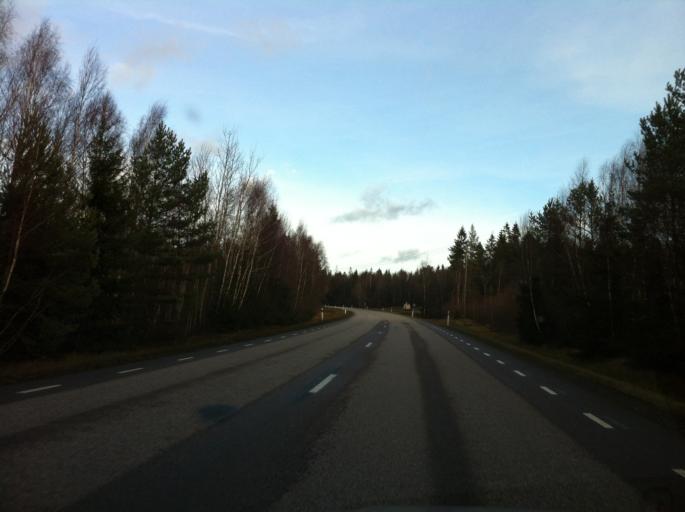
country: SE
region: Kronoberg
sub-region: Almhults Kommun
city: AElmhult
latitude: 56.5759
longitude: 14.1860
